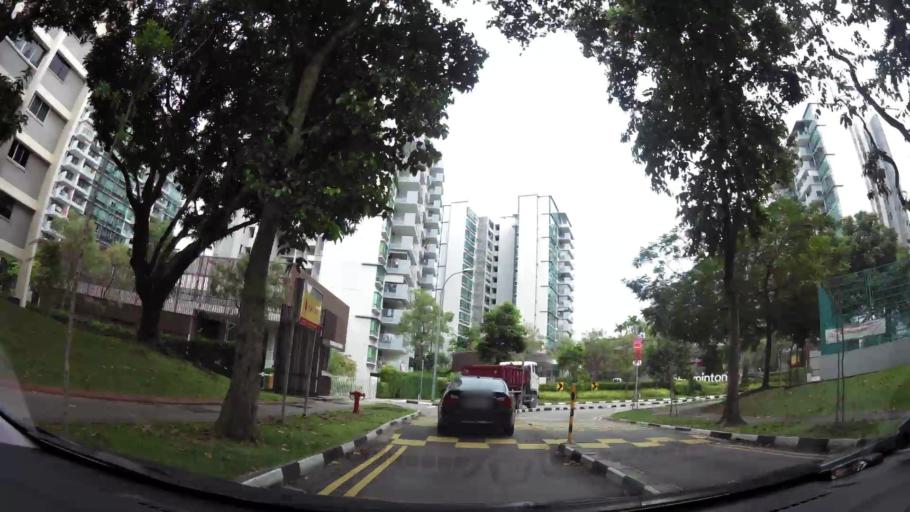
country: SG
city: Singapore
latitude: 1.3520
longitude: 103.8805
